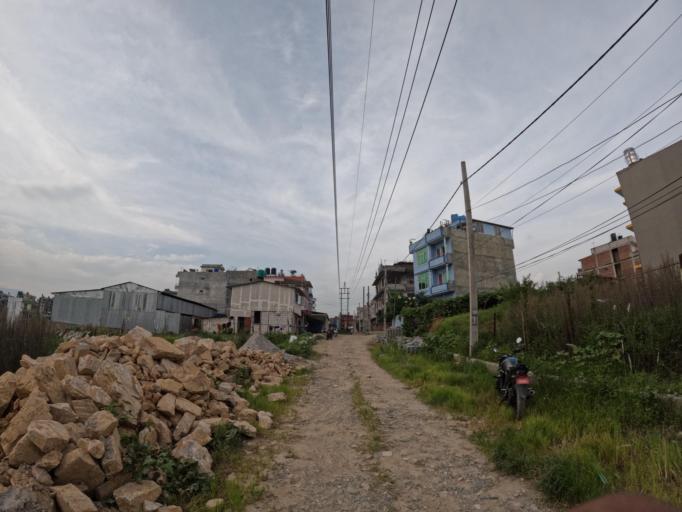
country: NP
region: Central Region
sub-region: Bagmati Zone
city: Bhaktapur
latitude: 27.6801
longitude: 85.3910
